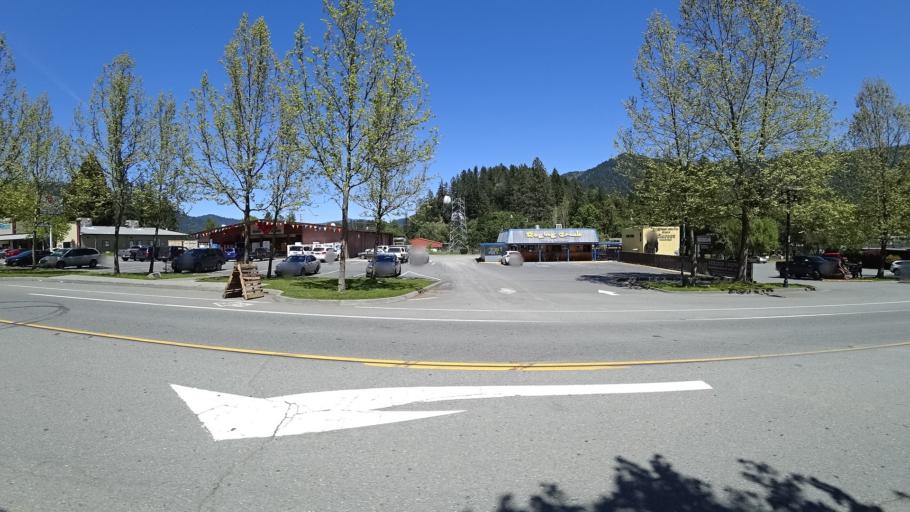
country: US
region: California
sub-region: Humboldt County
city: Willow Creek
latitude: 40.9397
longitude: -123.6328
